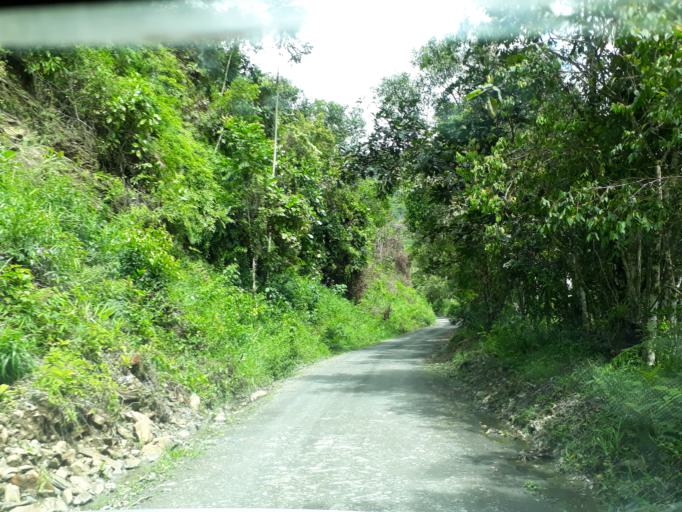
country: CO
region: Boyaca
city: Quipama
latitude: 5.4429
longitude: -74.1807
